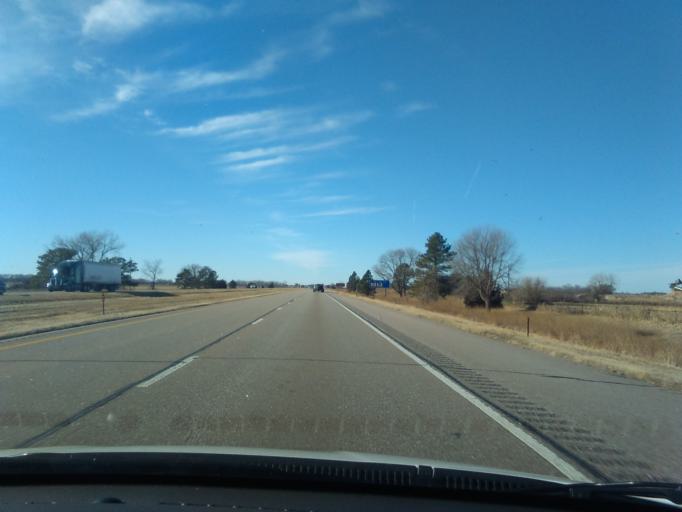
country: US
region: Nebraska
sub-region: Hall County
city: Wood River
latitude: 40.8043
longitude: -98.4729
